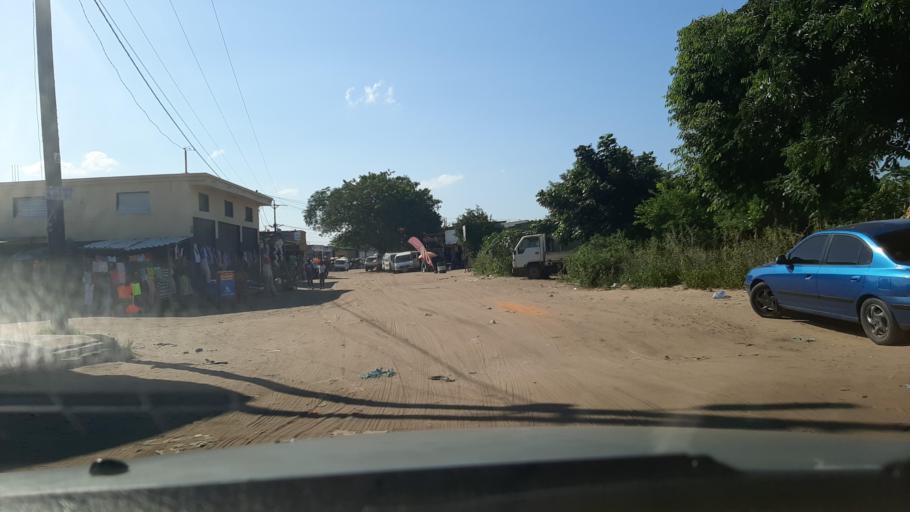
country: MZ
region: Maputo
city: Matola
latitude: -25.7929
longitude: 32.4885
